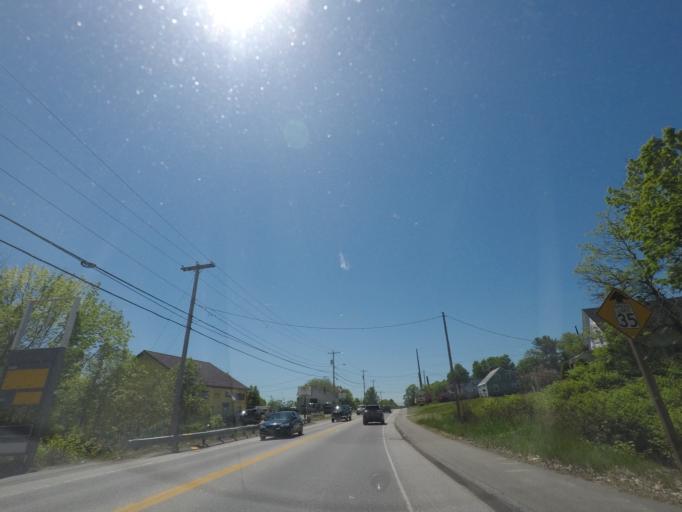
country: US
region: Maine
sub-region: Kennebec County
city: Farmingdale
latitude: 44.2563
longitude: -69.7732
